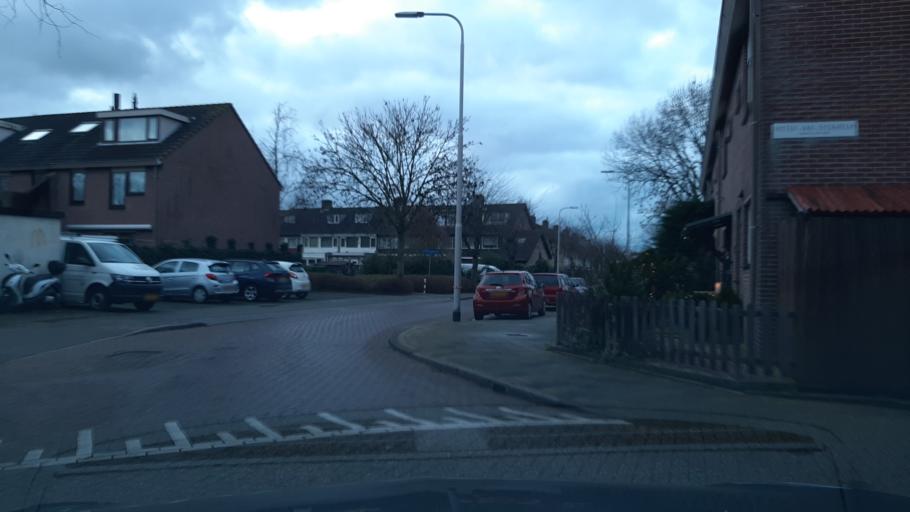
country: NL
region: South Holland
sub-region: Gemeente Hillegom
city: Hillegom
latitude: 52.2809
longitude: 4.5869
